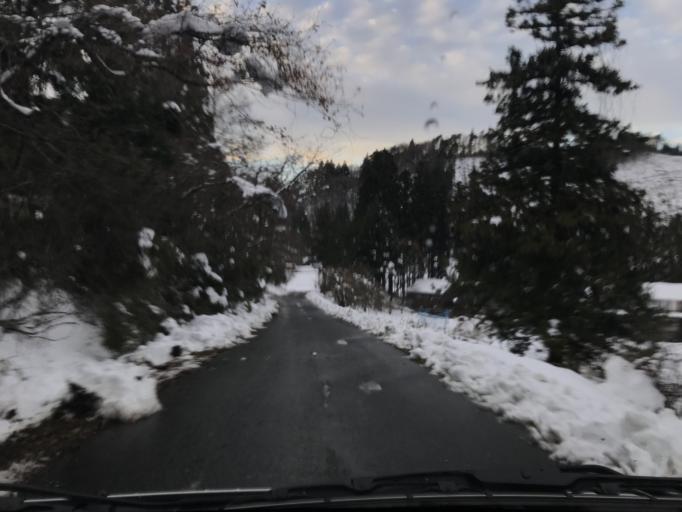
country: JP
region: Iwate
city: Mizusawa
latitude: 39.0461
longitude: 141.0190
